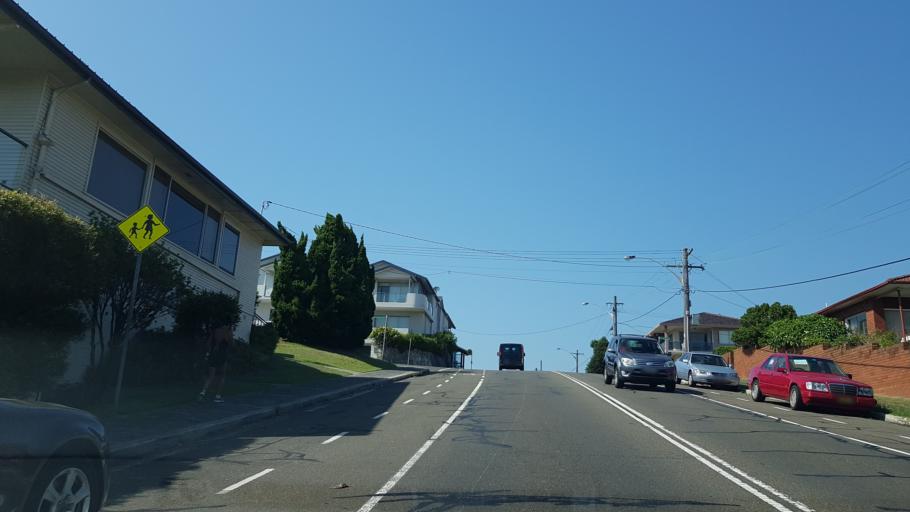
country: AU
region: New South Wales
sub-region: Warringah
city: North Curl Curl
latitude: -33.7593
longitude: 151.2960
